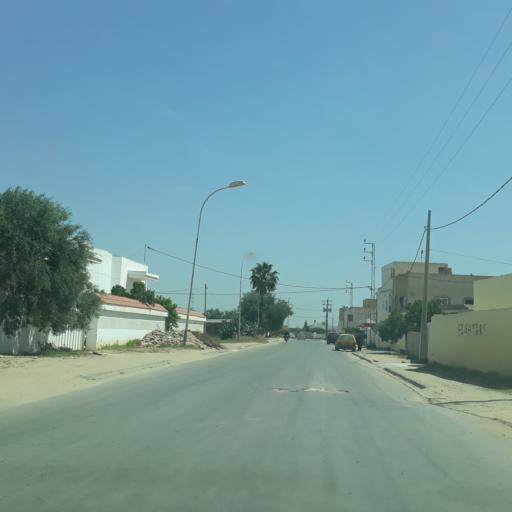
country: TN
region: Safaqis
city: Al Qarmadah
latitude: 34.8133
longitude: 10.7704
